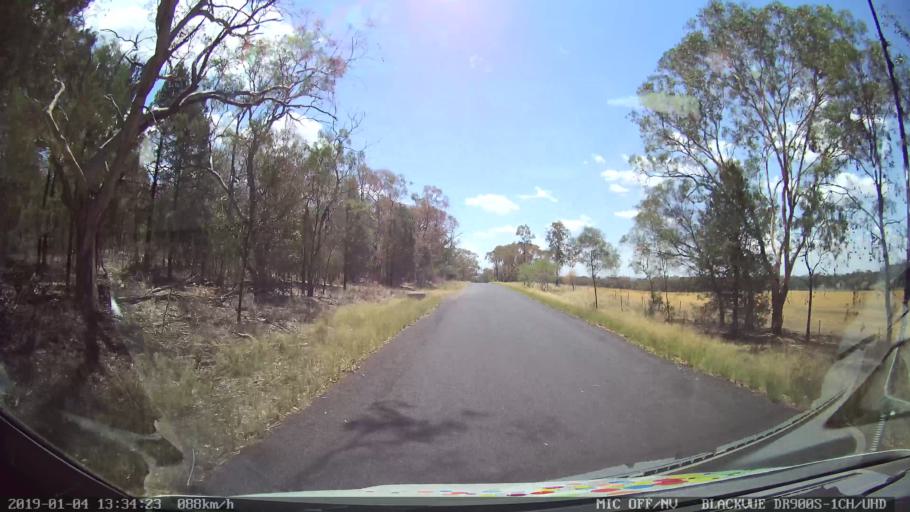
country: AU
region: New South Wales
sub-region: Dubbo Municipality
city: Dubbo
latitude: -32.5863
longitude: 148.5369
